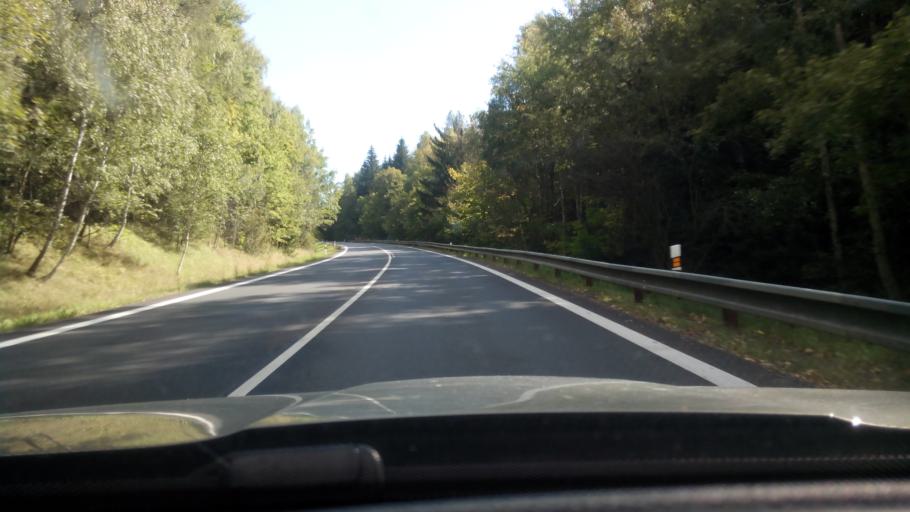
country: CZ
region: Jihocesky
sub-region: Okres Prachatice
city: Zdikov
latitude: 49.0758
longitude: 13.7054
